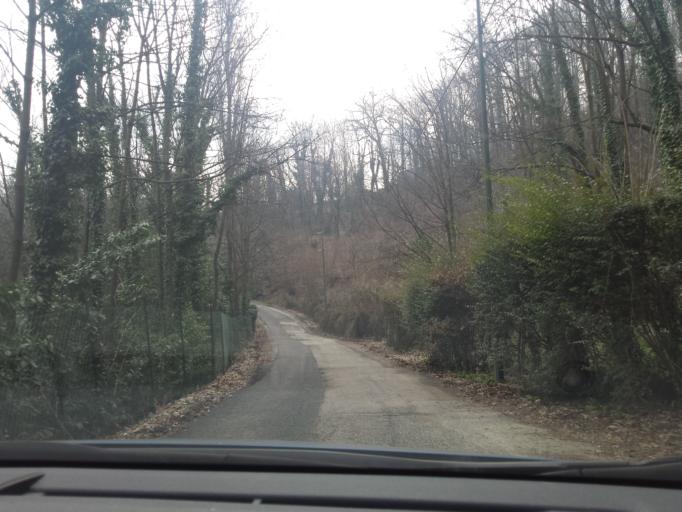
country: IT
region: Piedmont
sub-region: Provincia di Torino
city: Revigliasco
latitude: 45.0591
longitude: 7.7290
